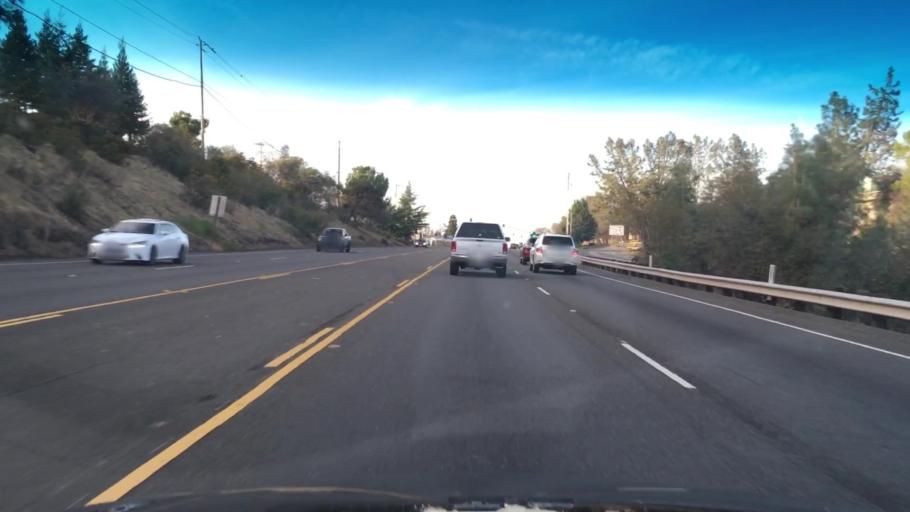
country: US
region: California
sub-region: Placer County
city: North Auburn
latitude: 38.9168
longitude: -121.0800
